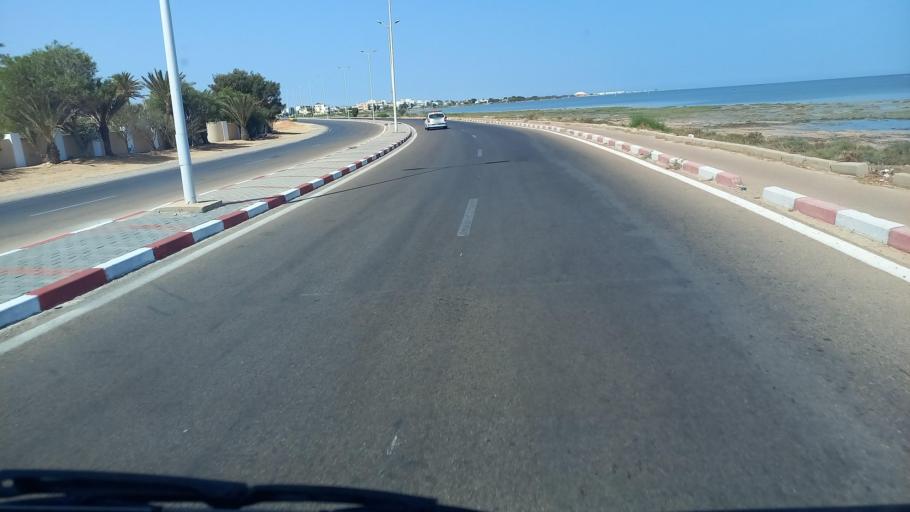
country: TN
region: Madanin
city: Houmt Souk
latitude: 33.8746
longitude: 10.9044
